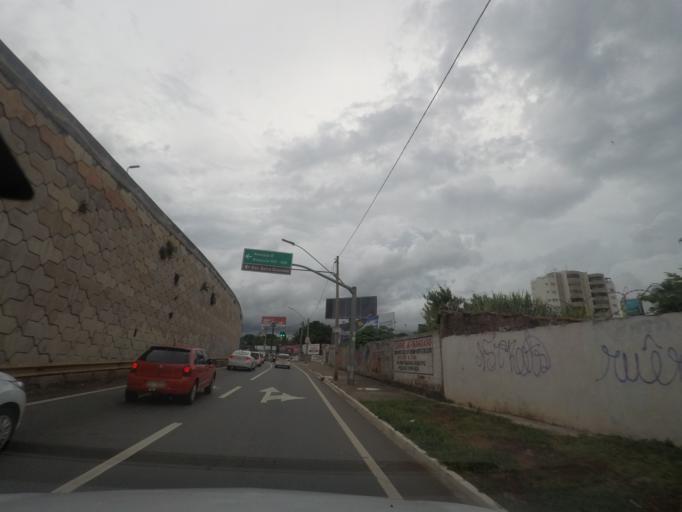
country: BR
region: Goias
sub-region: Goiania
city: Goiania
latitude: -16.6936
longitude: -49.2444
